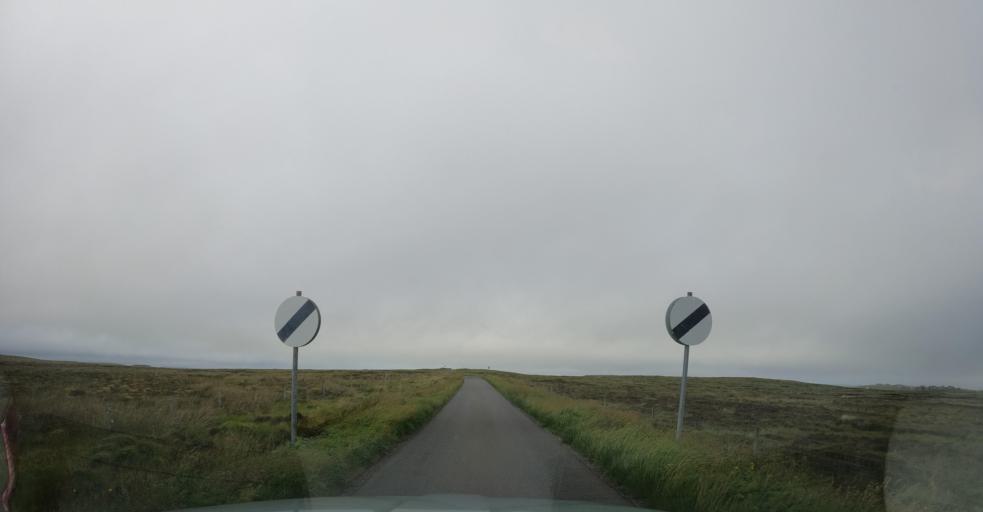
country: GB
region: Scotland
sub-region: Eilean Siar
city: Stornoway
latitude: 58.2022
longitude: -6.2327
